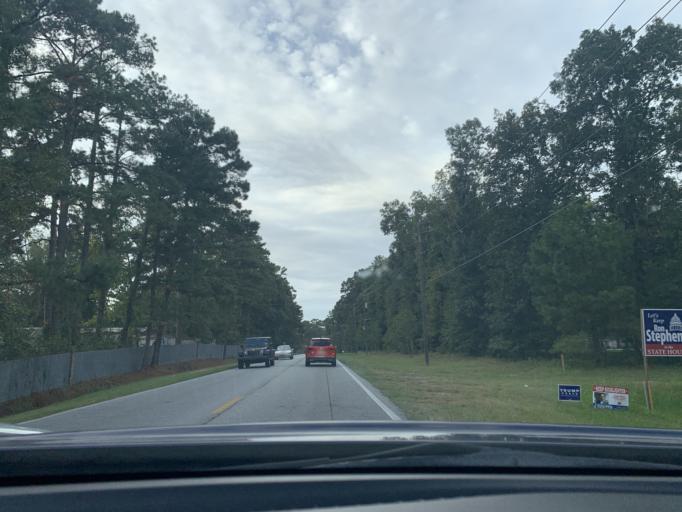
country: US
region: Georgia
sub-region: Chatham County
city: Georgetown
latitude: 32.0322
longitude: -81.2518
